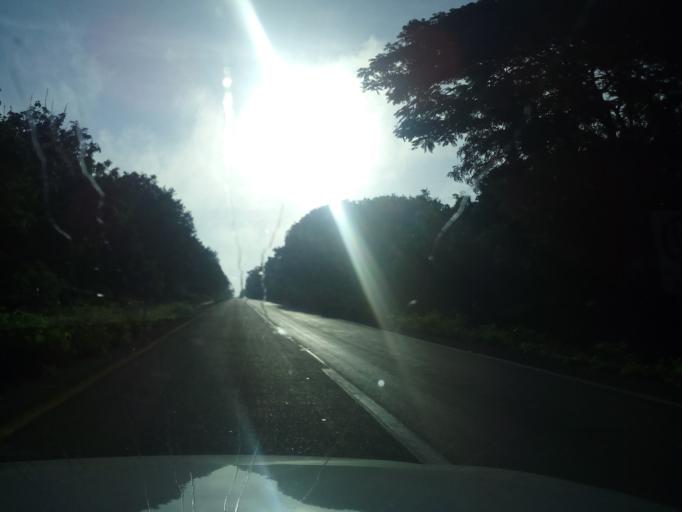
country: MX
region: Yucatan
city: Tunkas
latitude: 20.7647
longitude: -88.7974
